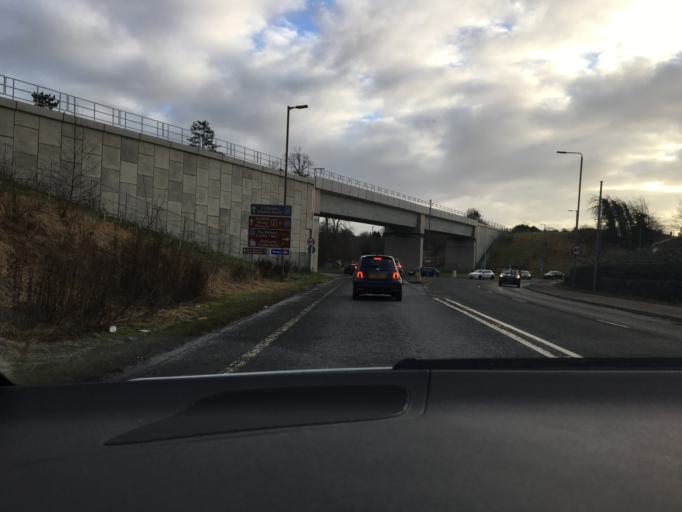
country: GB
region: Scotland
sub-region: Midlothian
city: Bonnyrigg
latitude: 55.8772
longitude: -3.0834
